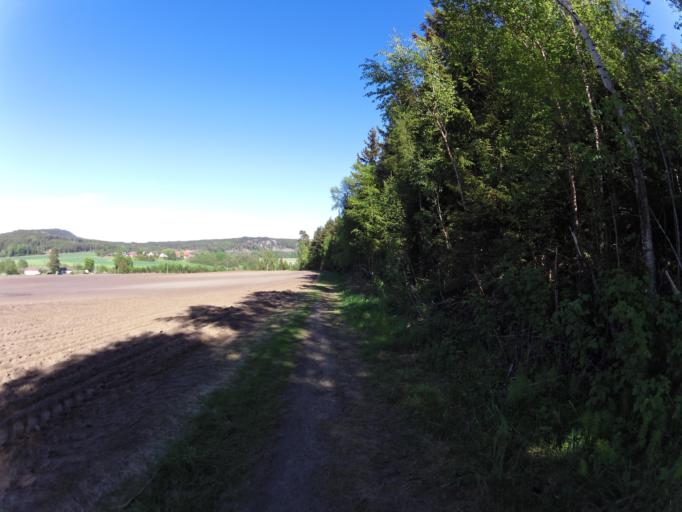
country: NO
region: Ostfold
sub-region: Sarpsborg
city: Sarpsborg
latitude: 59.2233
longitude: 11.0494
